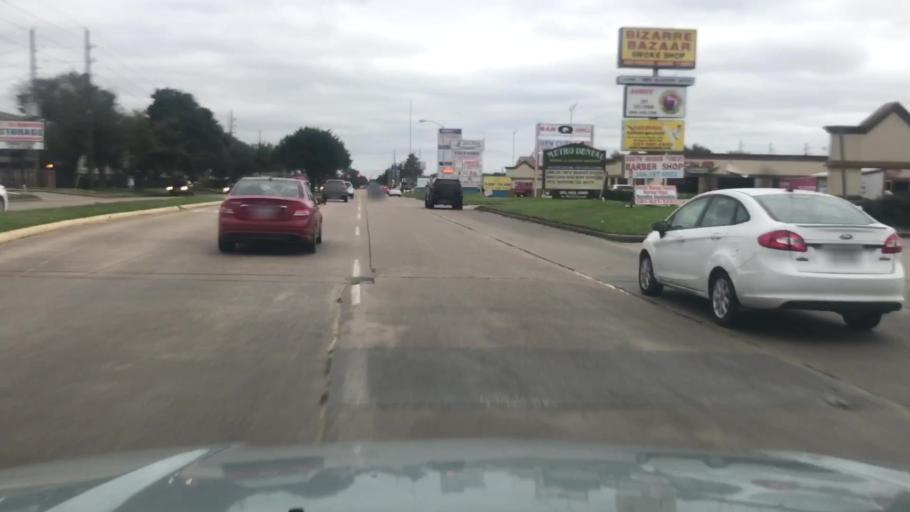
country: US
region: Texas
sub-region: Fort Bend County
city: Cinco Ranch
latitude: 29.7676
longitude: -95.7517
